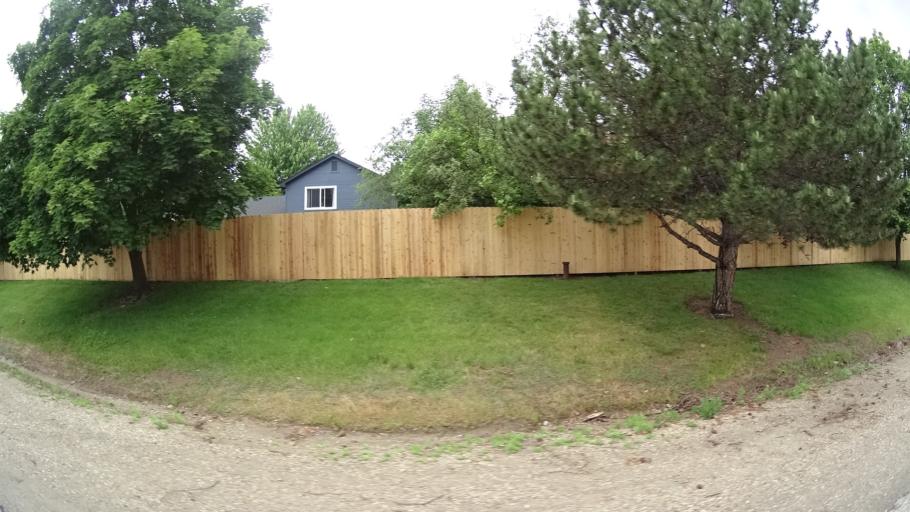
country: US
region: Idaho
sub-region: Ada County
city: Eagle
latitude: 43.7104
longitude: -116.3151
